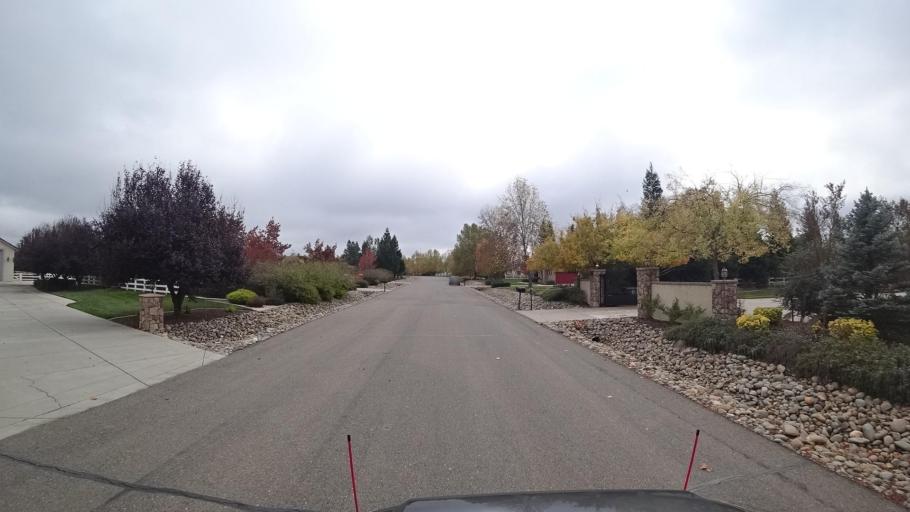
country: US
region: California
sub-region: Sacramento County
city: Vineyard
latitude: 38.4480
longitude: -121.3126
